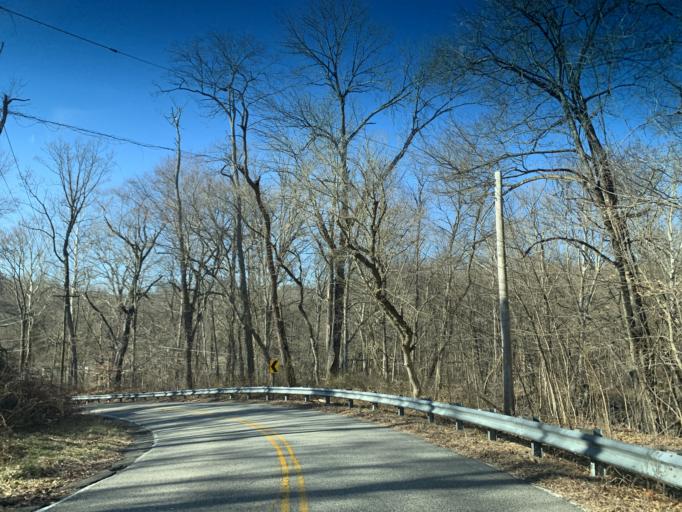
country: US
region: Maryland
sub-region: Cecil County
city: Rising Sun
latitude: 39.6546
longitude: -76.1163
